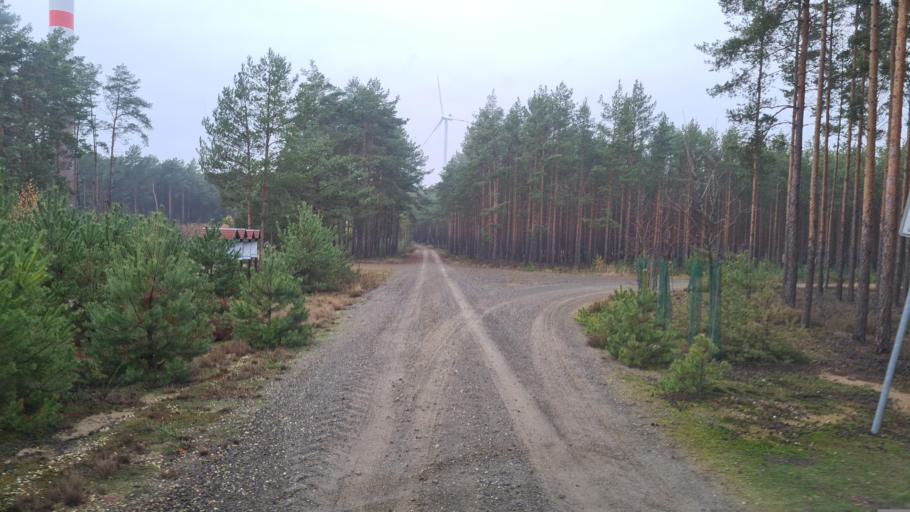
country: DE
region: Brandenburg
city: Sallgast
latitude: 51.6411
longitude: 13.8244
